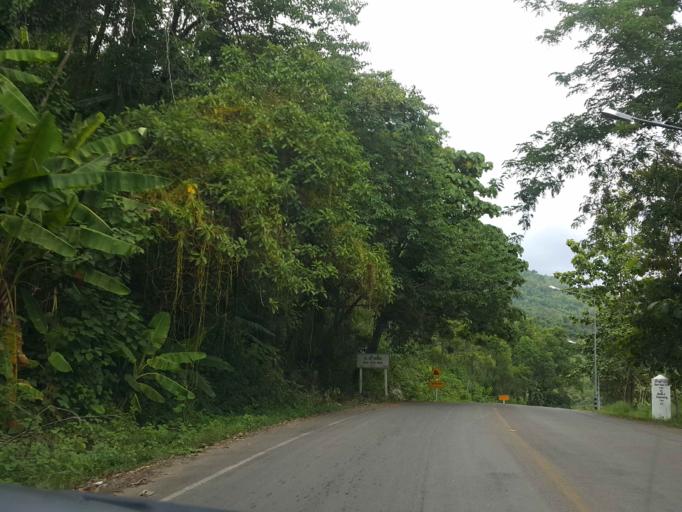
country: TH
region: Chiang Mai
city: Samoeng
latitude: 18.7866
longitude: 98.8412
